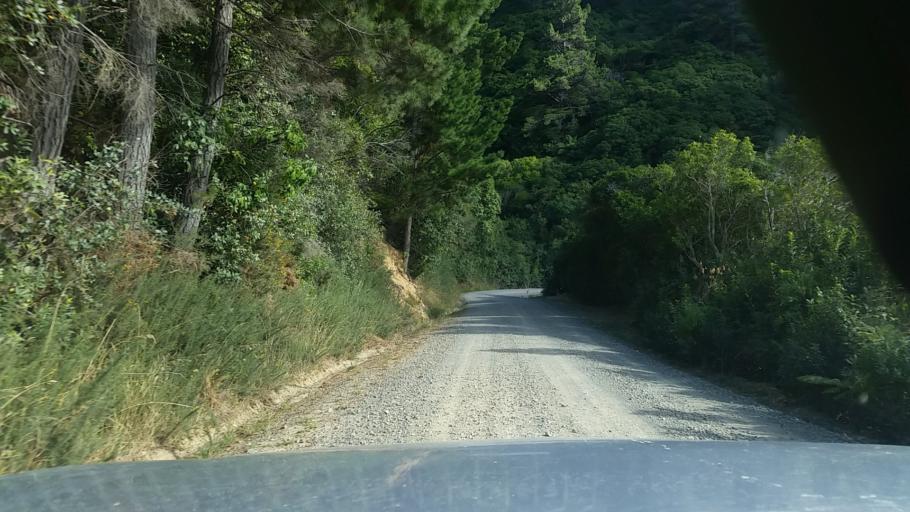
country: NZ
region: Marlborough
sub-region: Marlborough District
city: Picton
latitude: -41.2878
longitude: 174.1306
